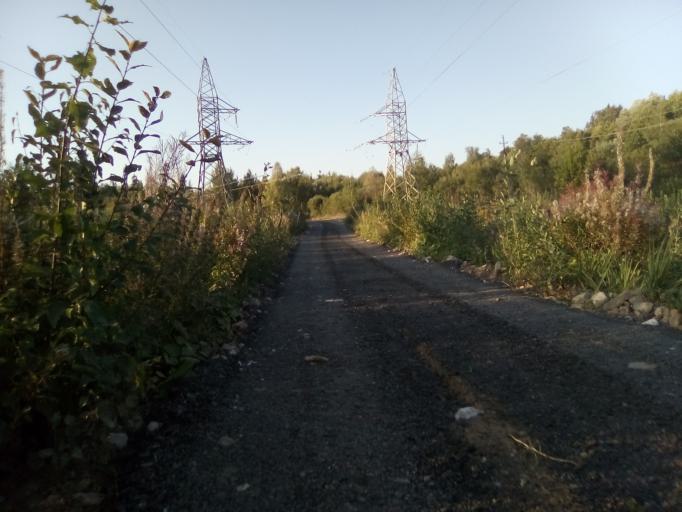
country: RU
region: Moskovskaya
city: Aprelevka
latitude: 55.5786
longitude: 37.0656
